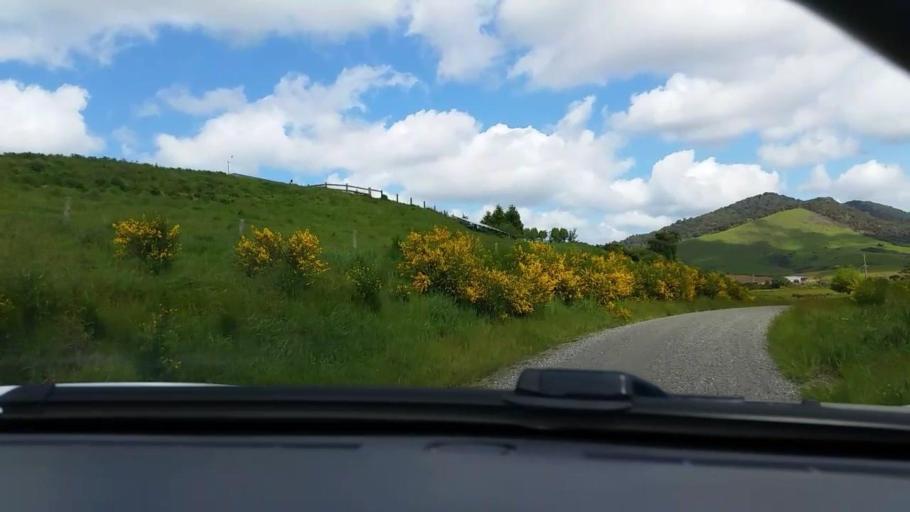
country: NZ
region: Otago
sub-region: Clutha District
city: Papatowai
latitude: -46.5904
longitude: 169.1462
